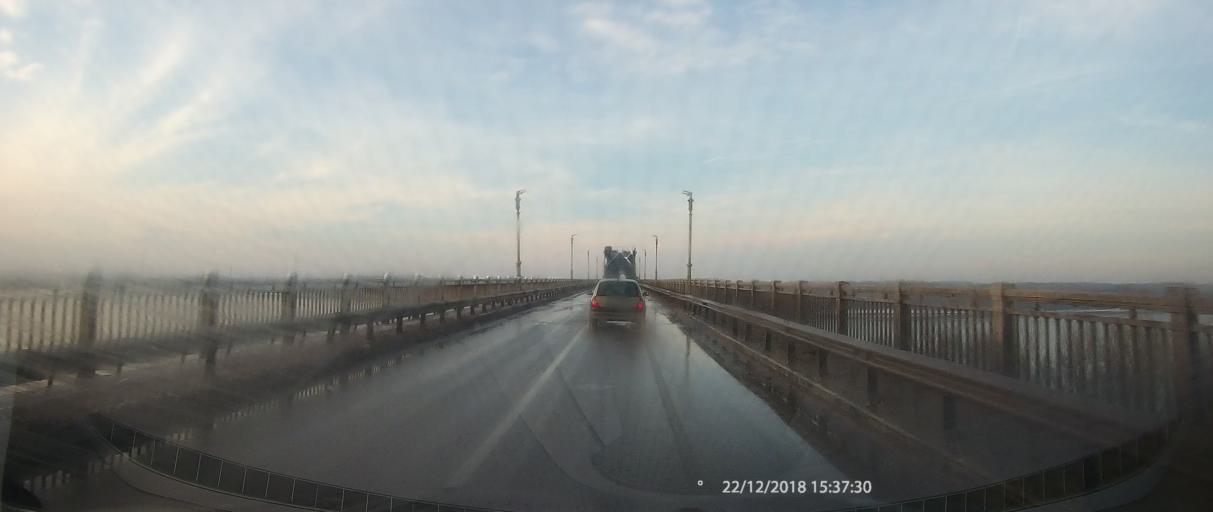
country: RO
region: Giurgiu
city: Giurgiu
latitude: 43.8841
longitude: 26.0106
